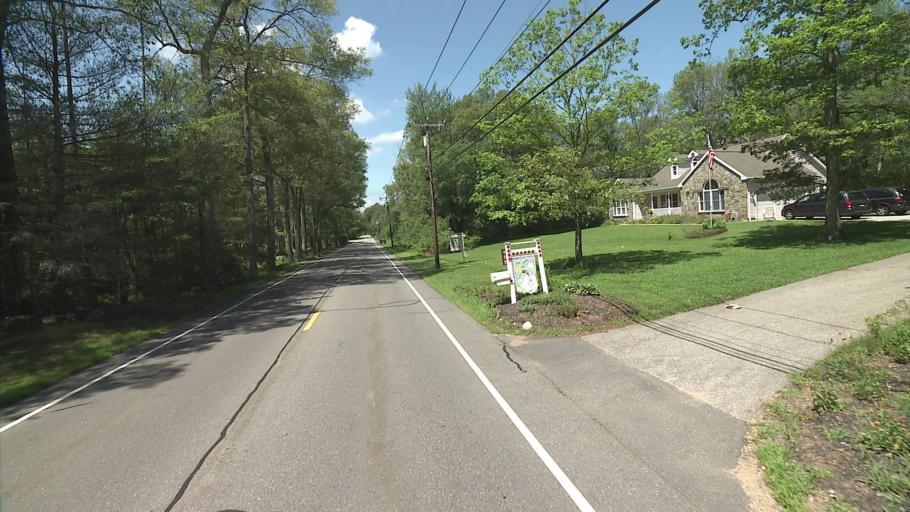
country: US
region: Connecticut
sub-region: New London County
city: Lisbon
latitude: 41.7097
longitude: -72.0270
